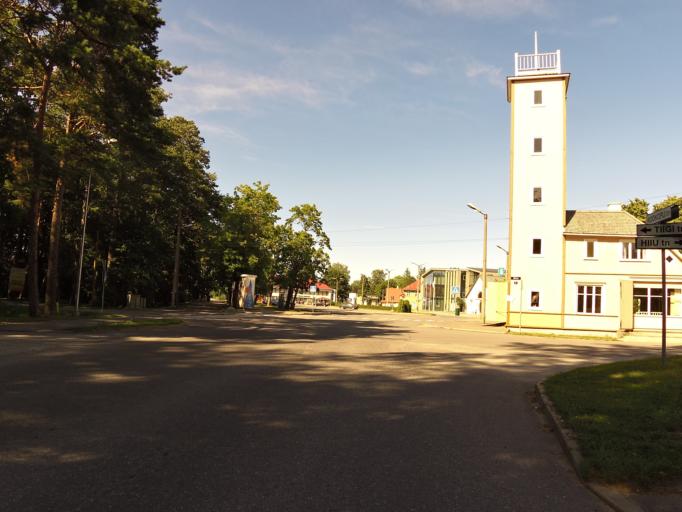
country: EE
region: Hiiumaa
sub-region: Kaerdla linn
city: Kardla
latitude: 58.9965
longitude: 22.7464
